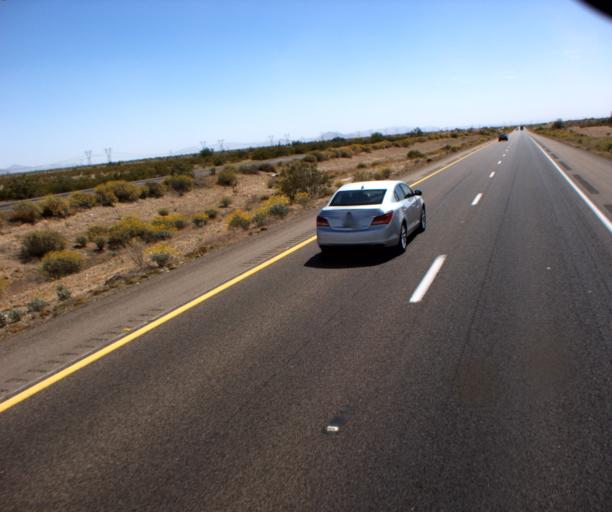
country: US
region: Arizona
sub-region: Maricopa County
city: Gila Bend
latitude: 33.0689
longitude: -112.6460
